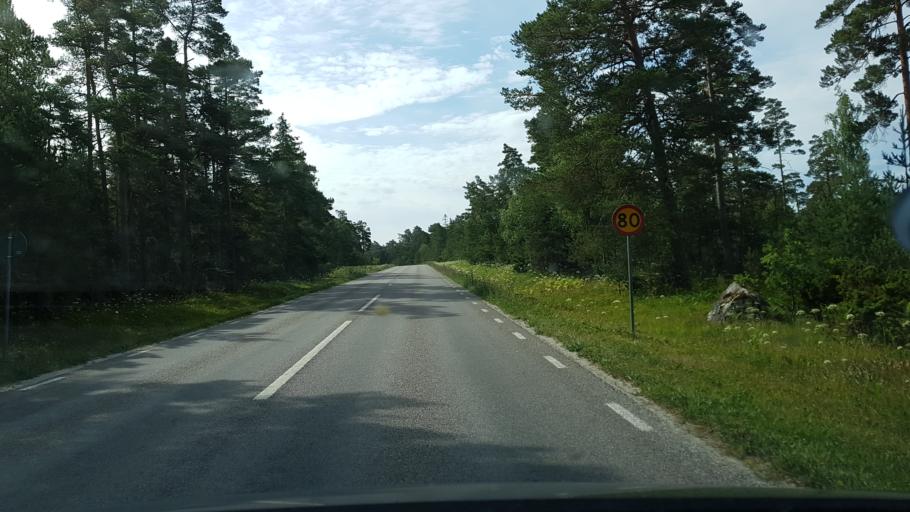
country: SE
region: Gotland
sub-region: Gotland
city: Hemse
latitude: 57.4628
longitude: 18.5720
